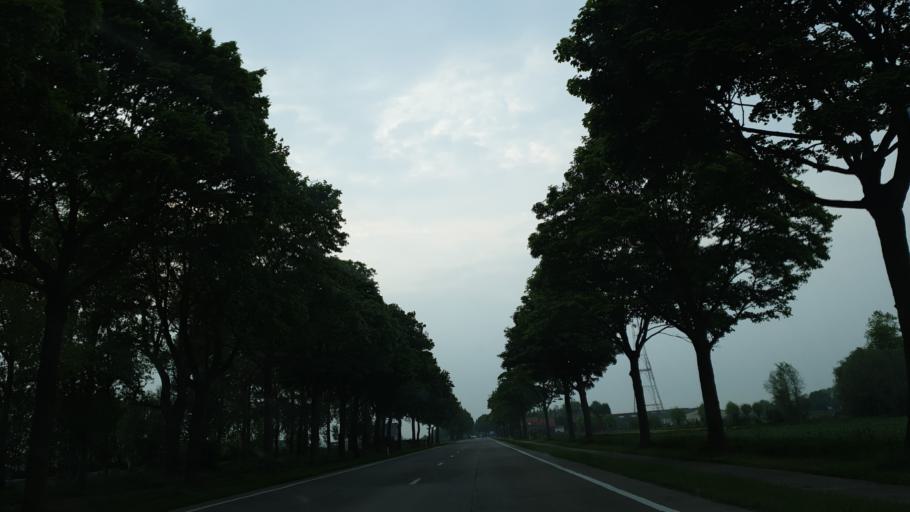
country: BE
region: Flanders
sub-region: Provincie West-Vlaanderen
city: Alveringem
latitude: 50.9390
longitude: 2.7300
